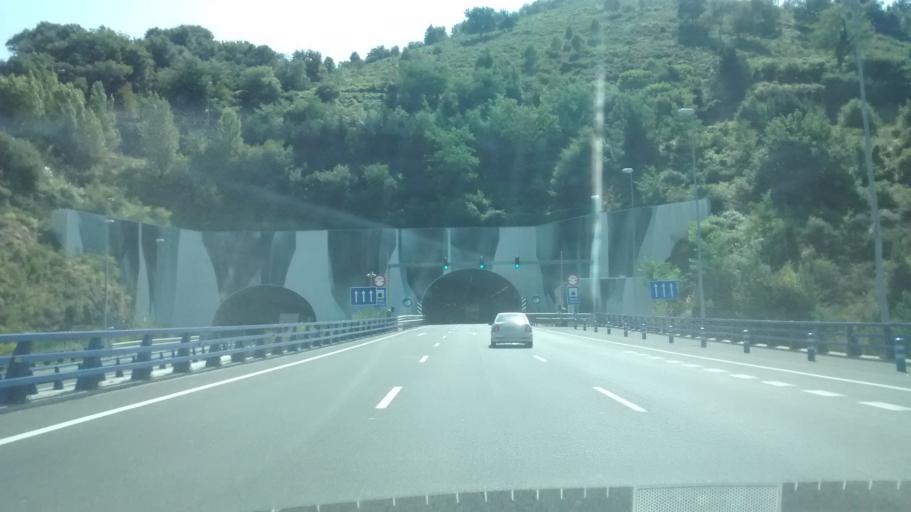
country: ES
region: Basque Country
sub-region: Bizkaia
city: Alonsotegi
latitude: 43.2510
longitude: -2.9744
